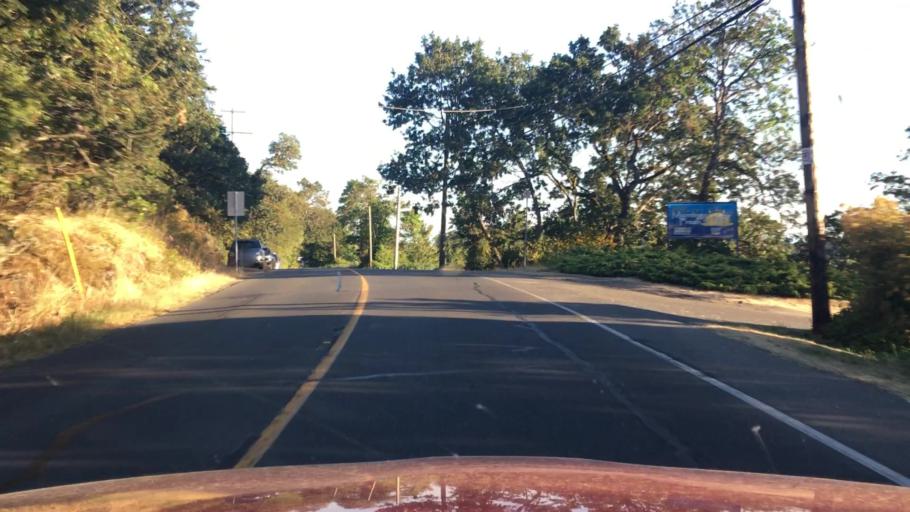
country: CA
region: British Columbia
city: Victoria
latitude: 48.4904
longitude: -123.3561
